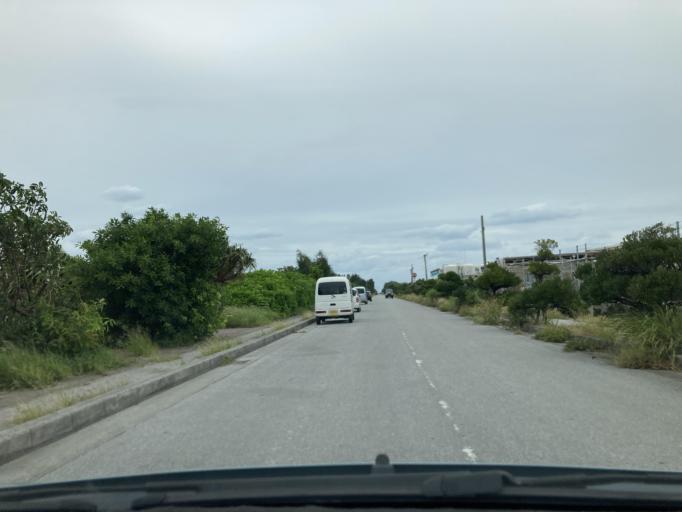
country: JP
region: Okinawa
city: Itoman
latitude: 26.1355
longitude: 127.6511
